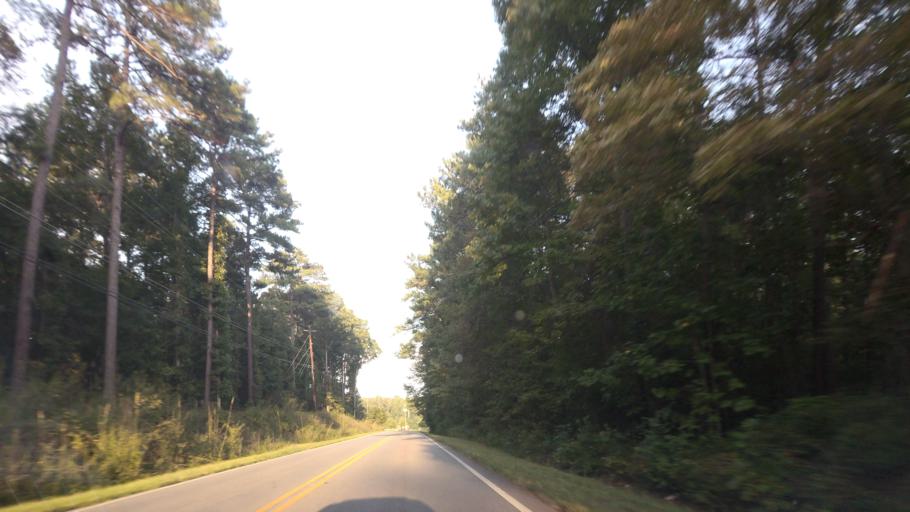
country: US
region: Georgia
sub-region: Bibb County
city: West Point
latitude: 32.8821
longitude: -83.7833
